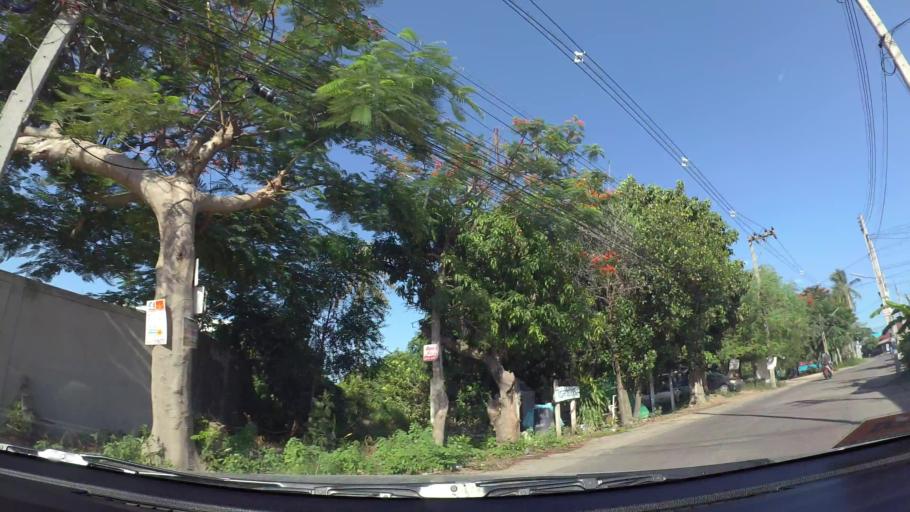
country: TH
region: Chon Buri
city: Si Racha
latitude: 13.1521
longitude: 100.9390
